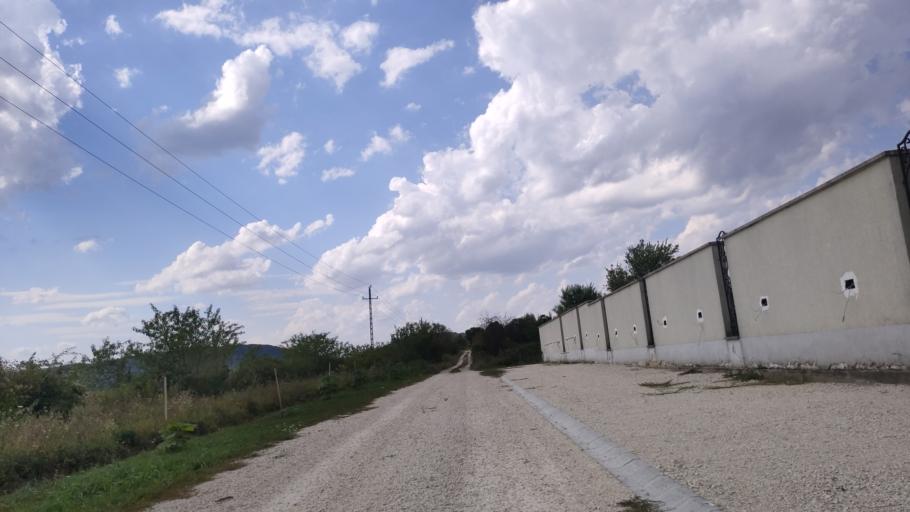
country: HU
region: Pest
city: Toeroekbalint
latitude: 47.4492
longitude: 18.8772
